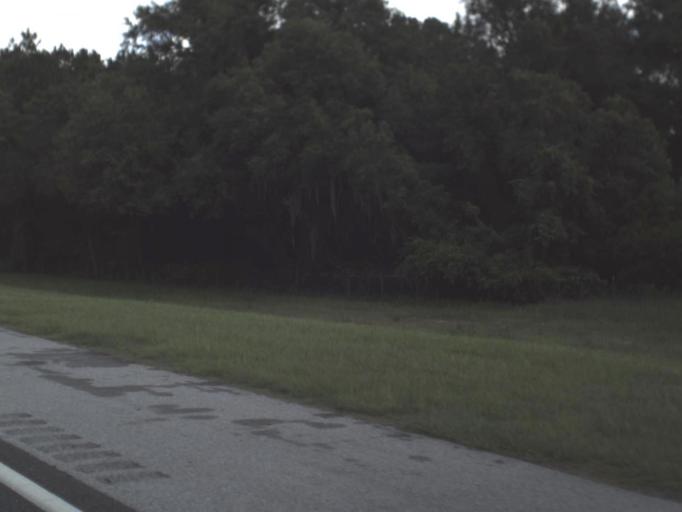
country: US
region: Florida
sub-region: Suwannee County
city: Wellborn
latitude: 30.3380
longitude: -82.8259
